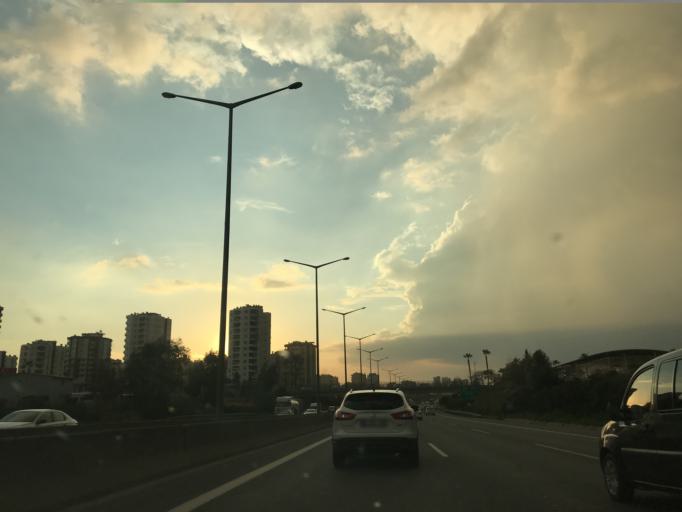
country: TR
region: Adana
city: Seyhan
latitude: 37.0304
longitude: 35.2766
